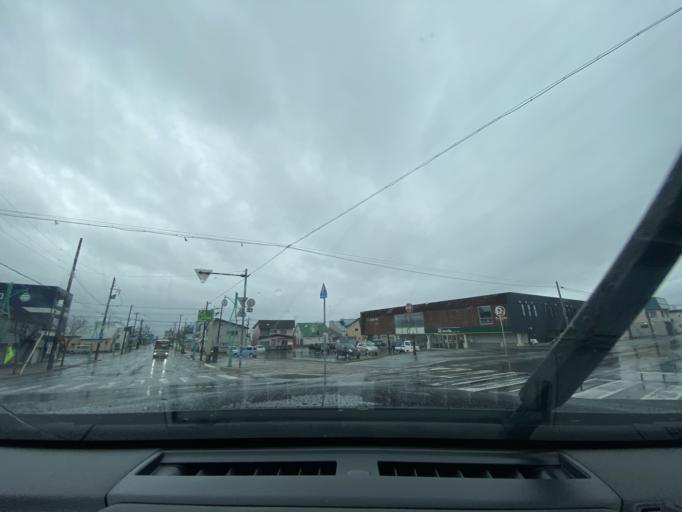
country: JP
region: Hokkaido
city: Fukagawa
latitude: 43.8098
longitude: 141.9324
